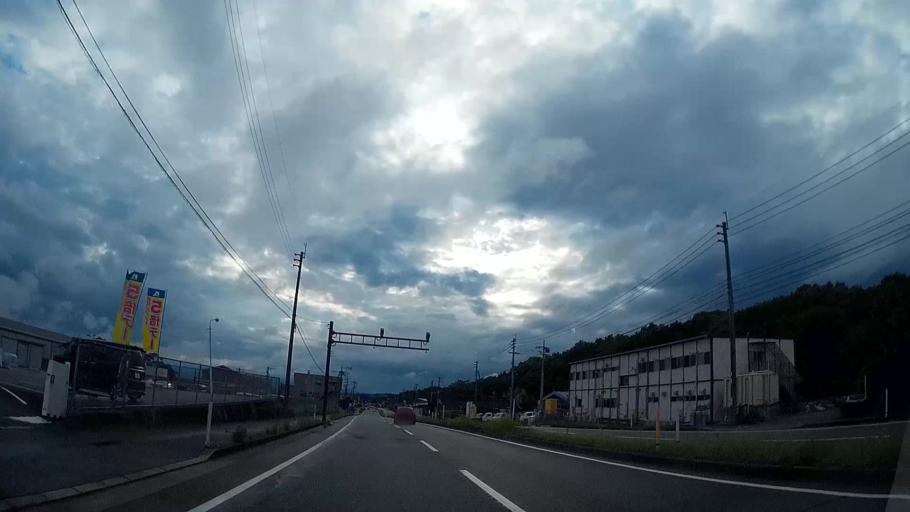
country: JP
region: Kumamoto
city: Ozu
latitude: 32.8802
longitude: 130.8999
